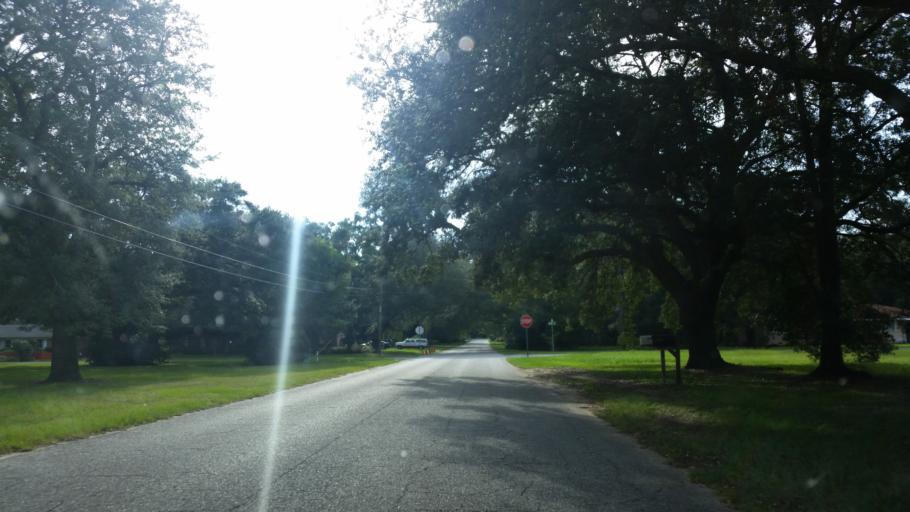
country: US
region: Florida
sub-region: Escambia County
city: Ferry Pass
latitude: 30.5047
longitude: -87.1914
